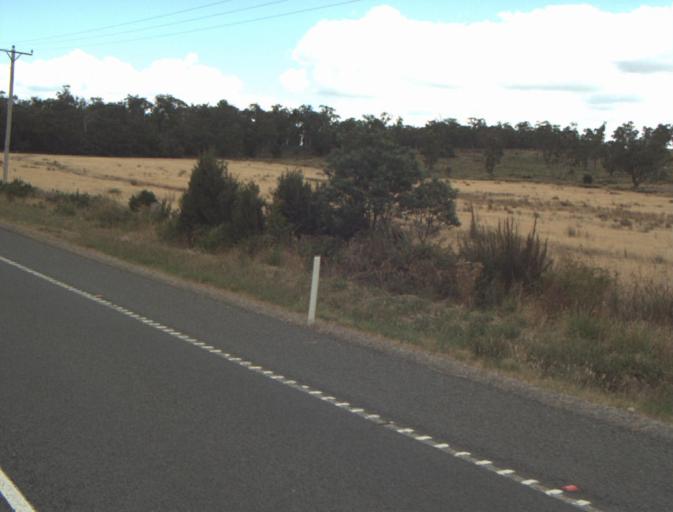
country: AU
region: Tasmania
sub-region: Launceston
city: Mayfield
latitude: -41.2539
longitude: 147.0235
